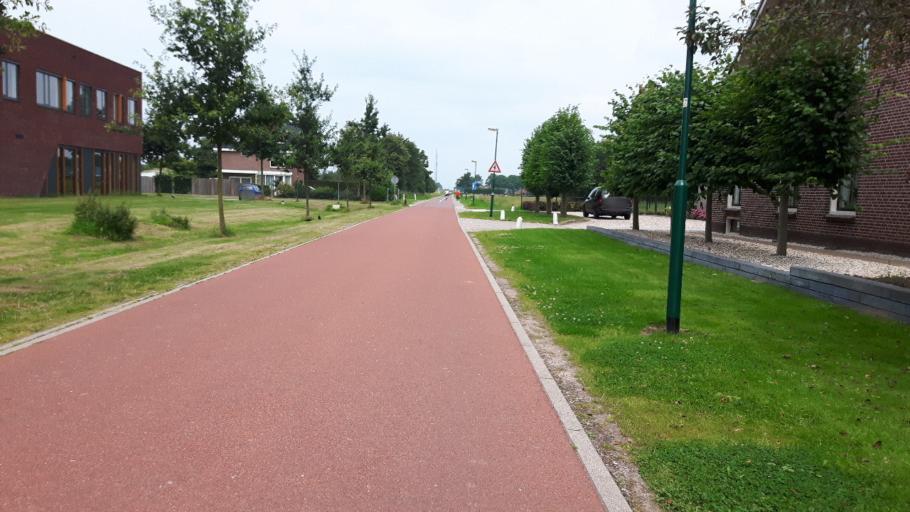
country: NL
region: Utrecht
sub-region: Gemeente Houten
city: Houten
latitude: 52.0291
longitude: 5.1843
